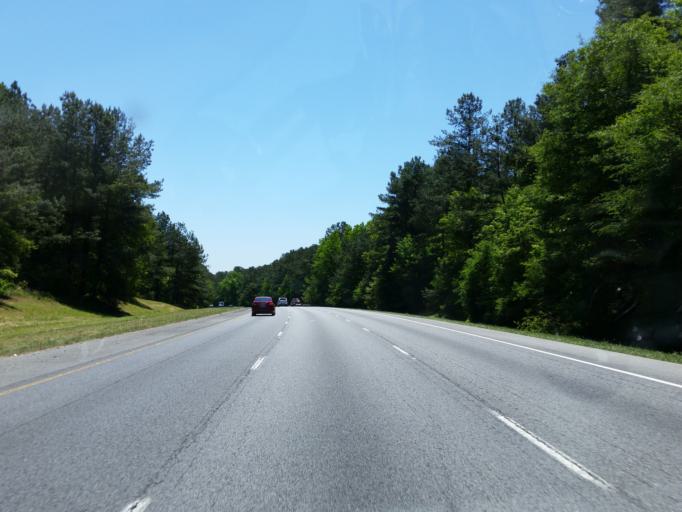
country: US
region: Georgia
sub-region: Monroe County
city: Forsyth
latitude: 33.0883
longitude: -83.9966
